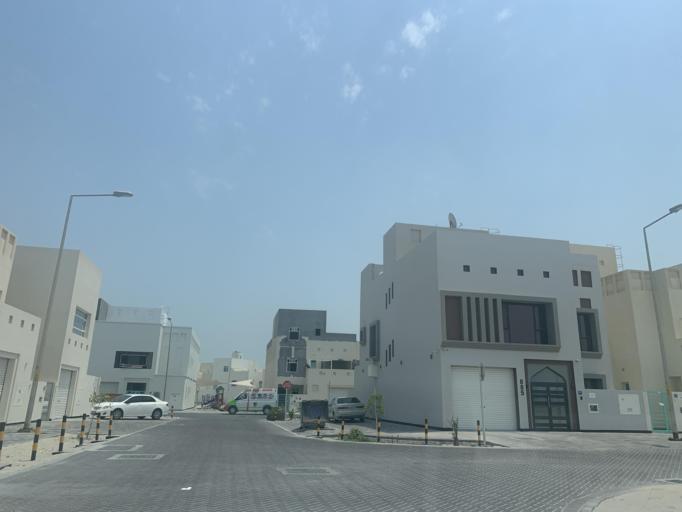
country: BH
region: Muharraq
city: Al Hadd
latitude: 26.2327
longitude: 50.6692
